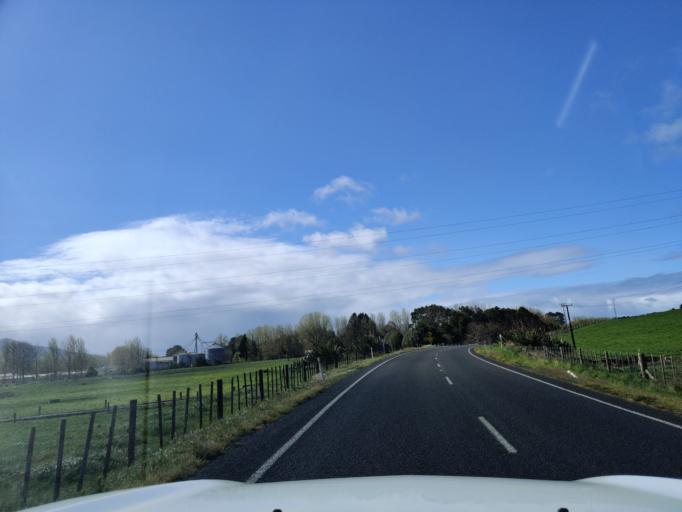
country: NZ
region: Waikato
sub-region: Otorohanga District
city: Otorohanga
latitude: -38.0684
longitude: 175.1749
